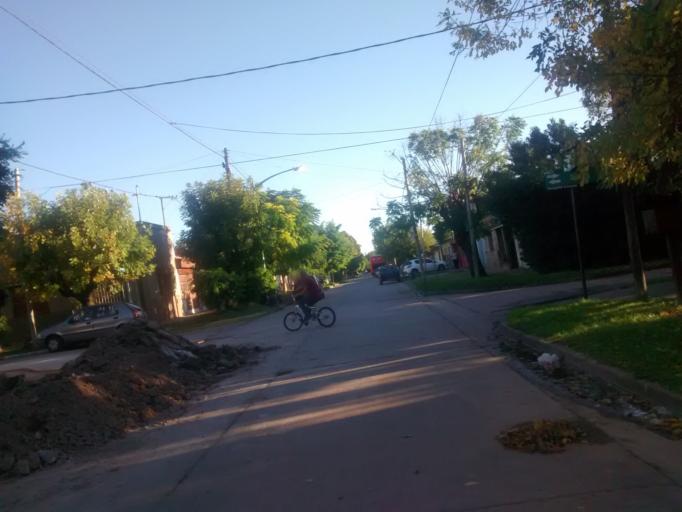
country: AR
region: Buenos Aires
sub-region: Partido de La Plata
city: La Plata
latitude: -34.8957
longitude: -57.9315
